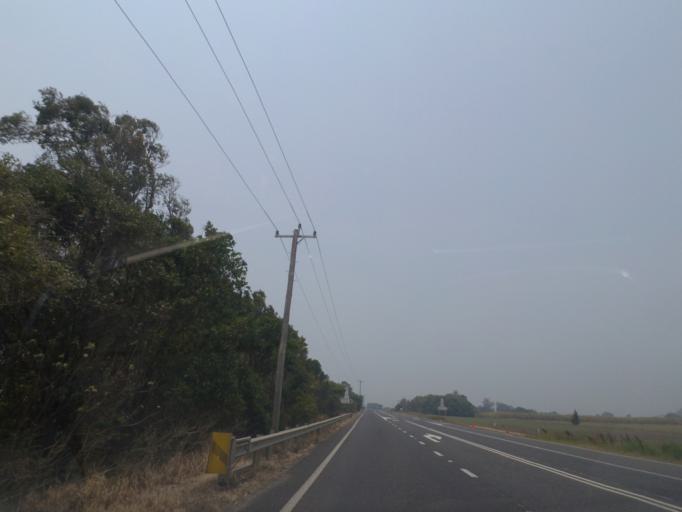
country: AU
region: New South Wales
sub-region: Richmond Valley
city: Evans Head
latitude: -28.9989
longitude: 153.4432
